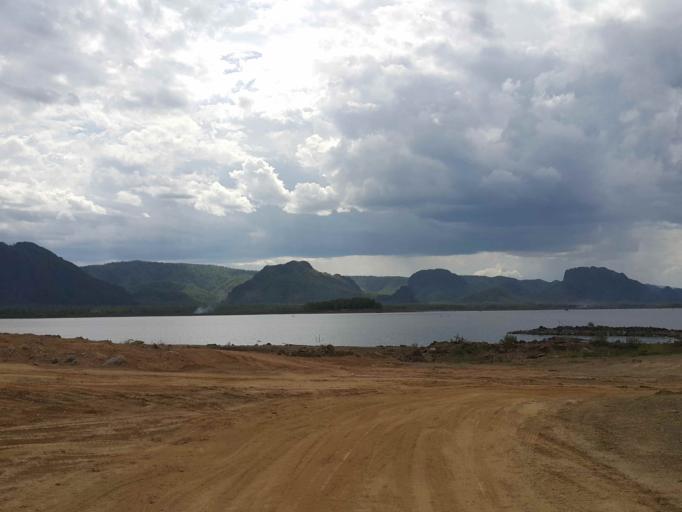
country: TH
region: Sukhothai
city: Thung Saliam
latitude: 17.3103
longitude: 99.4241
